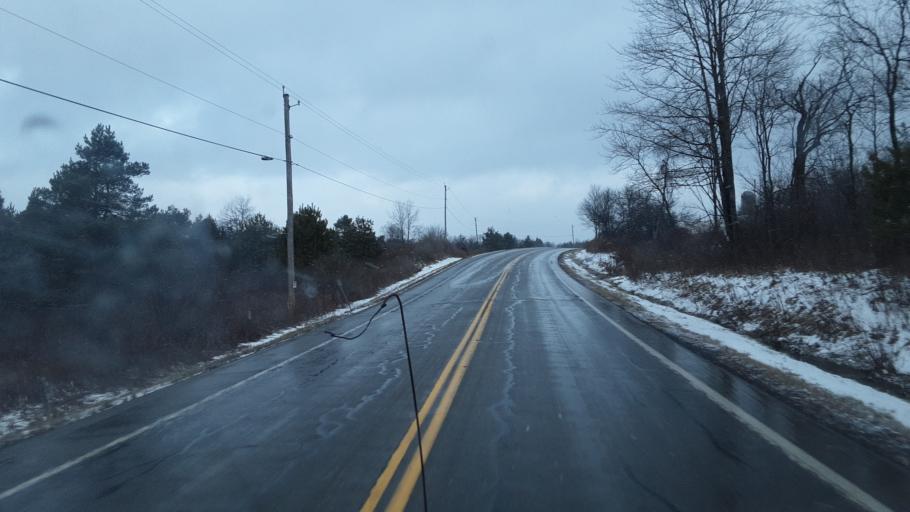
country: US
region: New York
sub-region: Allegany County
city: Houghton
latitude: 42.3216
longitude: -78.1229
